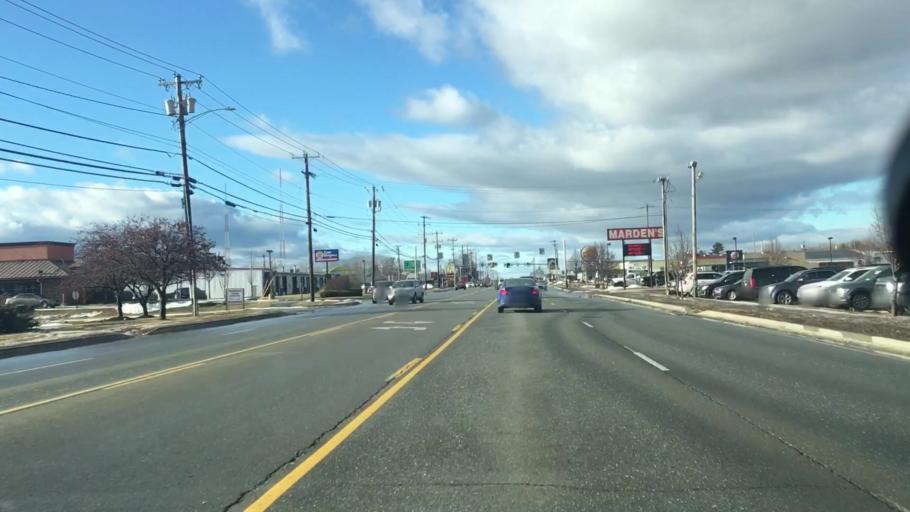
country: US
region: Maine
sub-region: Penobscot County
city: Brewer
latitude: 44.7794
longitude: -68.7402
